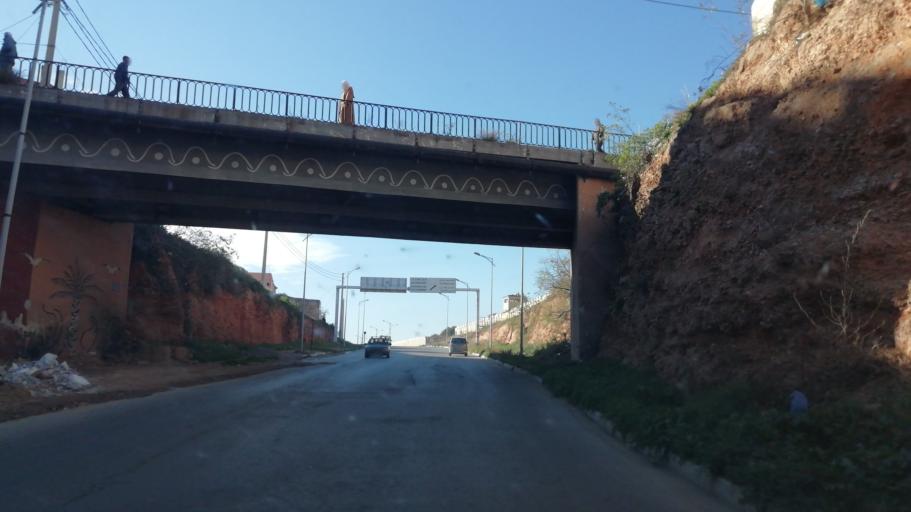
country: DZ
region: Oran
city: Oran
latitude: 35.6861
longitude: -0.6700
